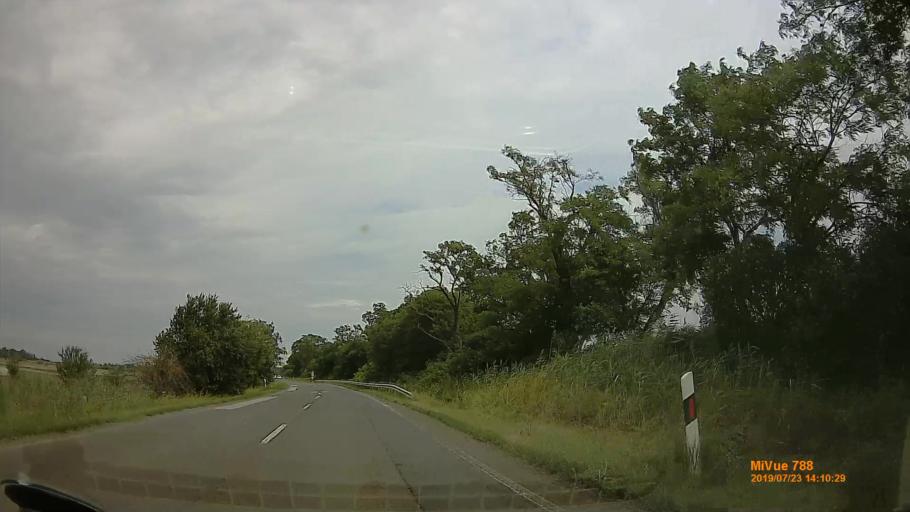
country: HU
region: Szabolcs-Szatmar-Bereg
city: Tiszalok
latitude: 47.9585
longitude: 21.4173
